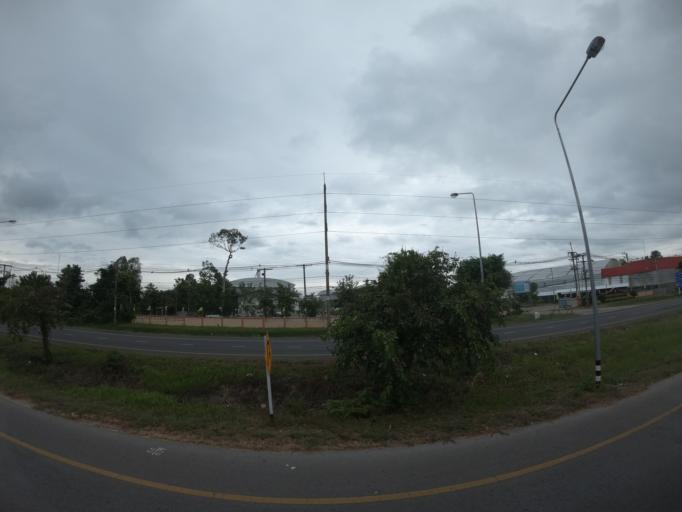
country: TH
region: Roi Et
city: Roi Et
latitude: 16.0442
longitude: 103.6284
